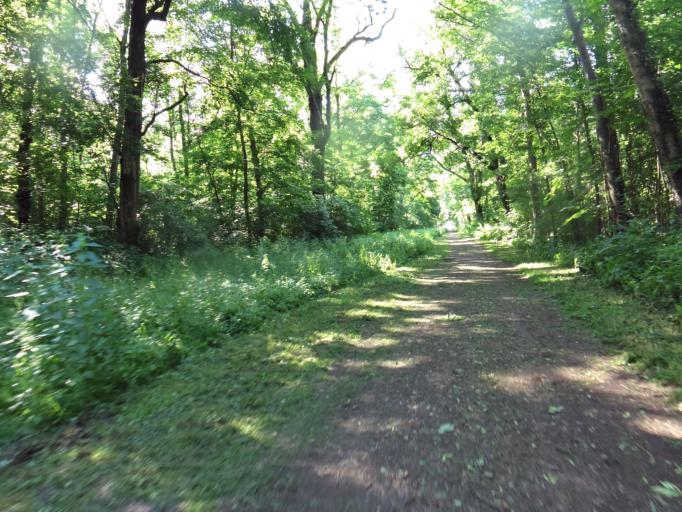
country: DE
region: Saxony
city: Leipzig
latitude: 51.3536
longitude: 12.3586
